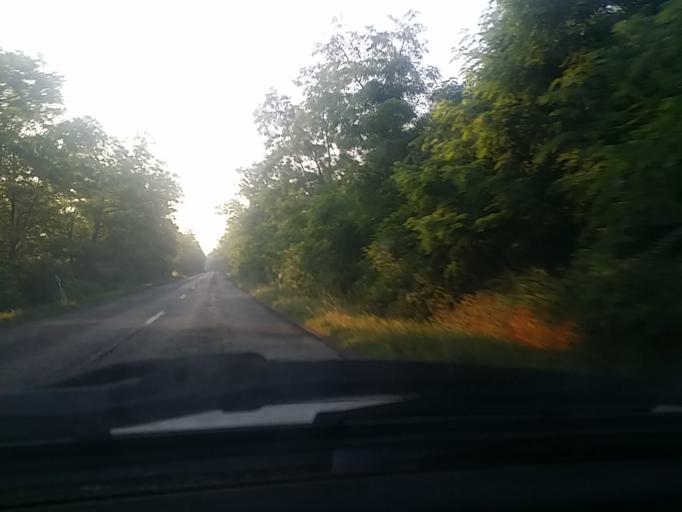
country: HU
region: Pest
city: Forropuszta
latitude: 47.4602
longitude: 19.6592
